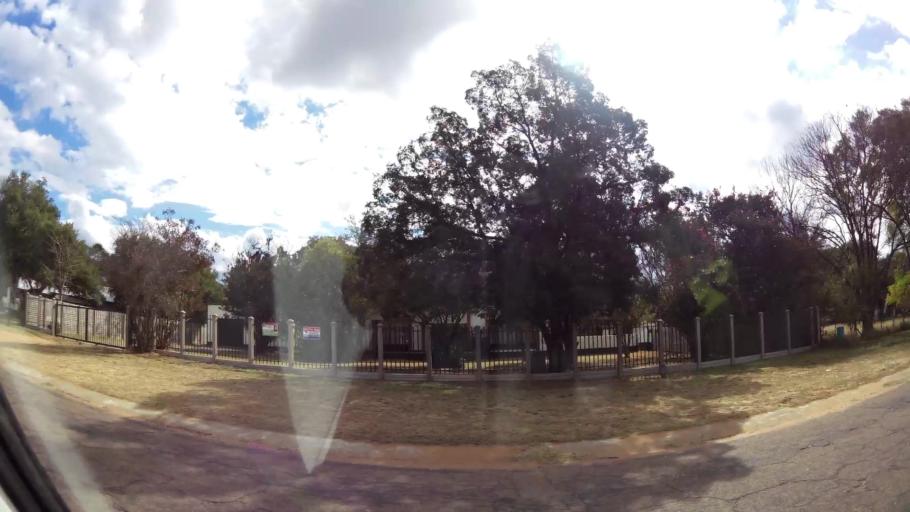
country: ZA
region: Limpopo
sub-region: Waterberg District Municipality
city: Modimolle
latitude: -24.7089
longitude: 28.4088
